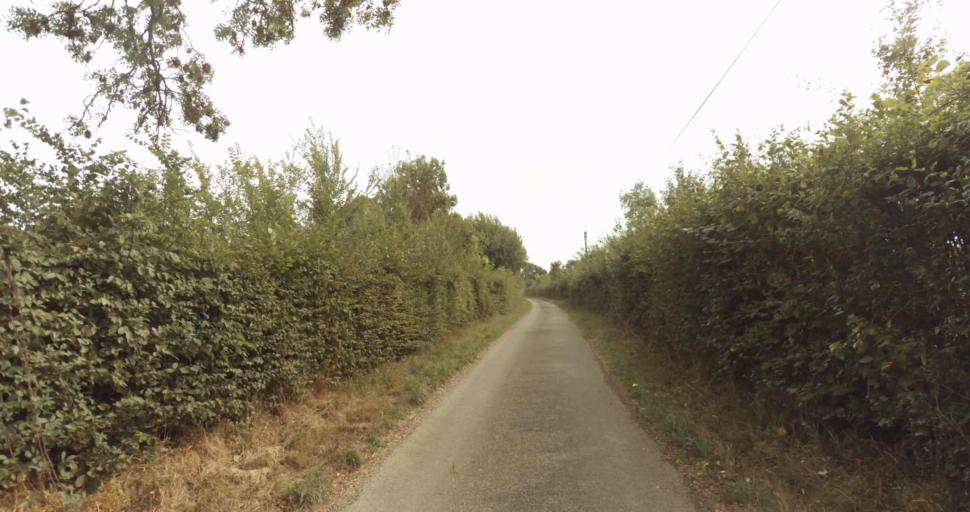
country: FR
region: Lower Normandy
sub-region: Departement de l'Orne
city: Gace
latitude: 48.8335
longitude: 0.3025
